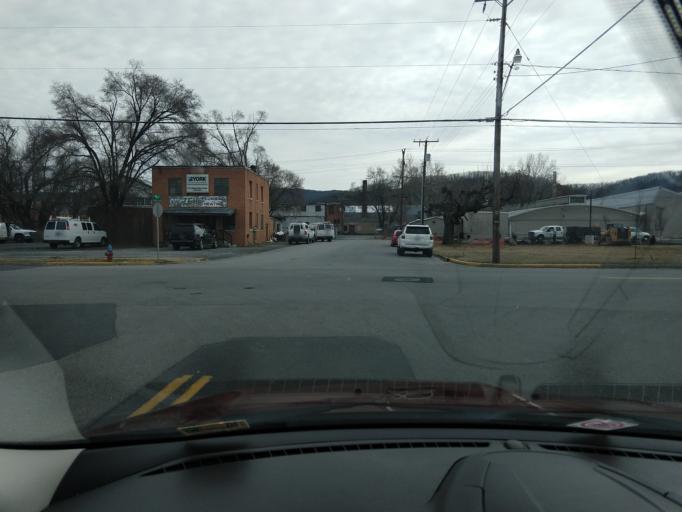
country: US
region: Virginia
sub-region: City of Waynesboro
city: Waynesboro
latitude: 38.0650
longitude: -78.8884
